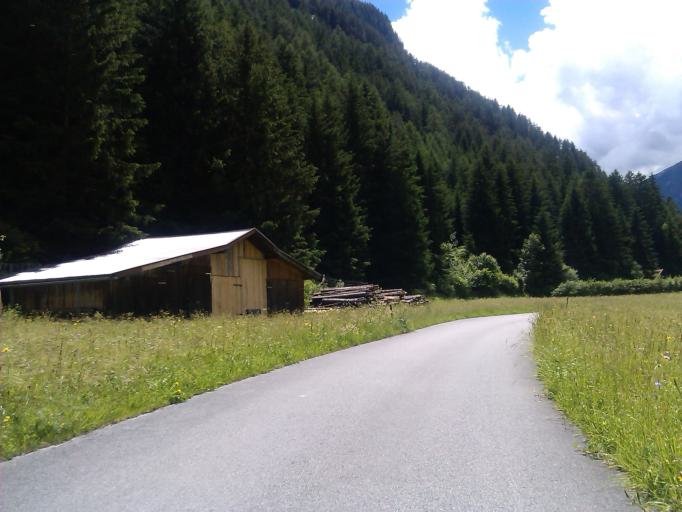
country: AT
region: Tyrol
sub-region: Politischer Bezirk Landeck
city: Pfunds
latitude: 46.9598
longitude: 10.5283
